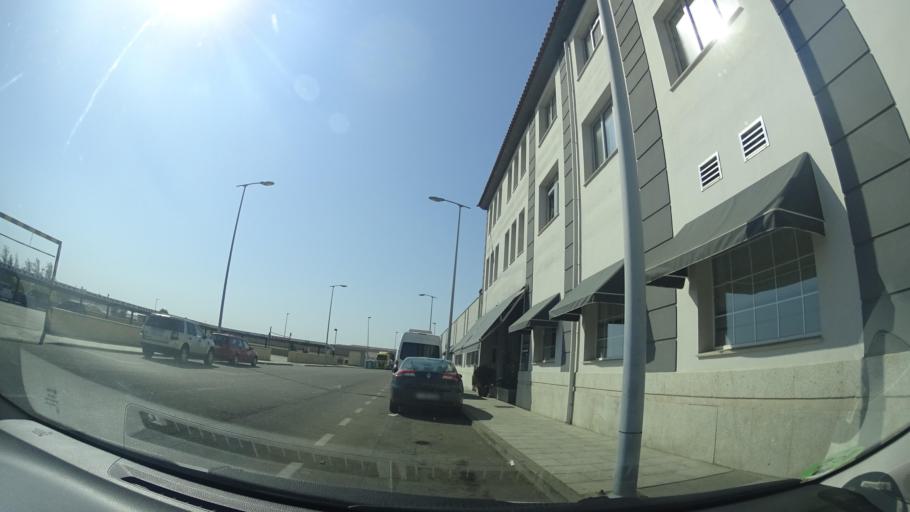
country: ES
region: Extremadura
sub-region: Provincia de Caceres
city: Miajadas
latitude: 39.1433
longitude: -5.9251
